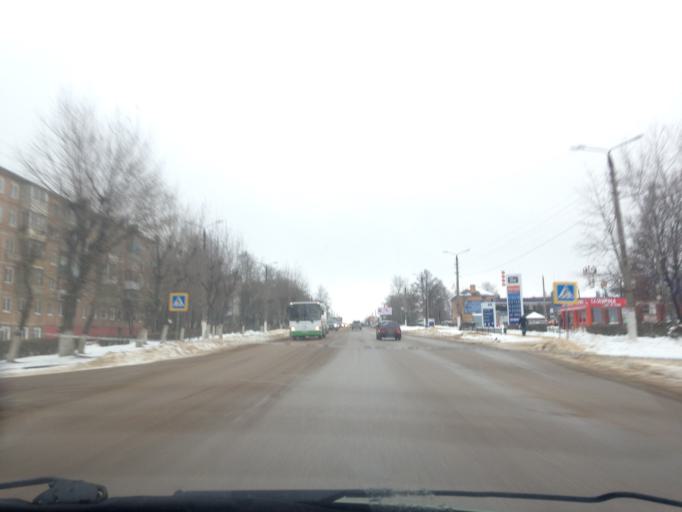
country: RU
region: Tula
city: Shchekino
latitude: 54.0156
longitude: 37.5163
